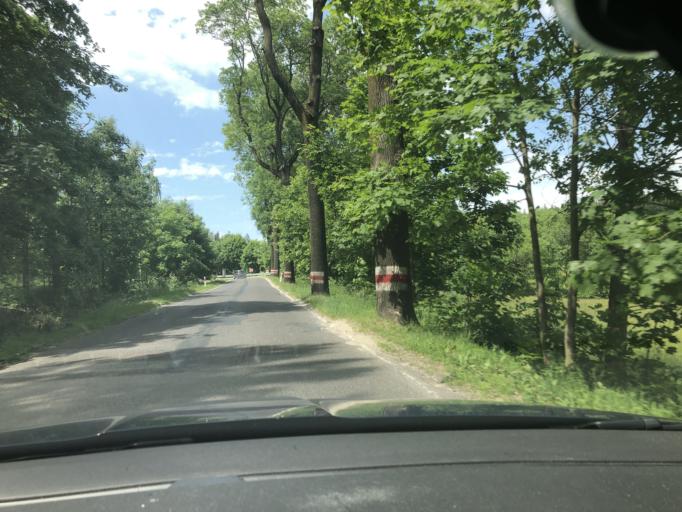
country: PL
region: Lower Silesian Voivodeship
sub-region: Powiat zlotoryjski
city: Swierzawa
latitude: 50.9660
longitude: 15.8307
